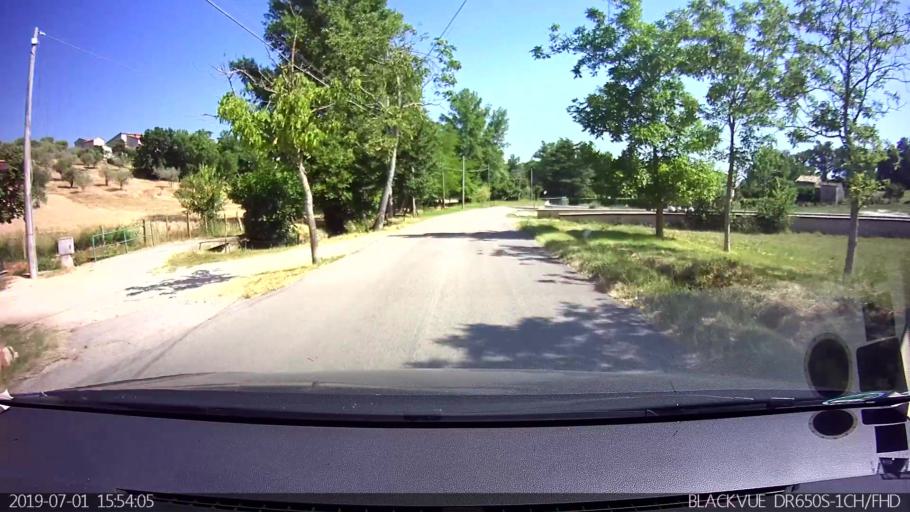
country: IT
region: Latium
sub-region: Provincia di Frosinone
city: Veroli
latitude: 41.6974
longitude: 13.4278
